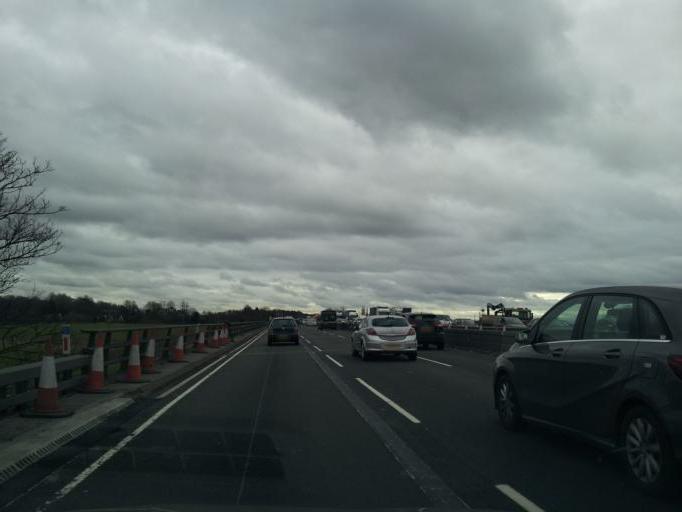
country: GB
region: England
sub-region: Staffordshire
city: Penkridge
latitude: 52.7407
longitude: -2.0987
